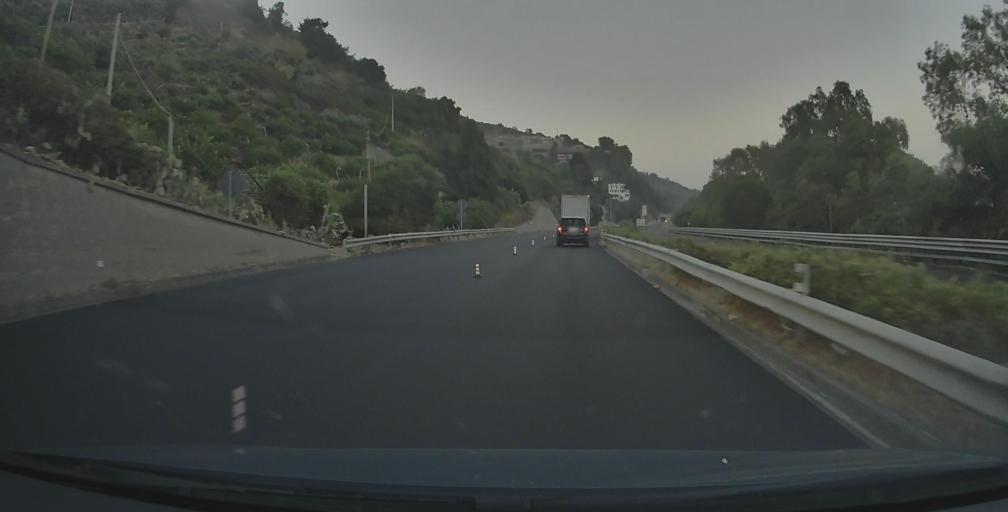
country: IT
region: Sicily
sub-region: Messina
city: Guidomandri Marina
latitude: 38.0371
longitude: 15.4518
